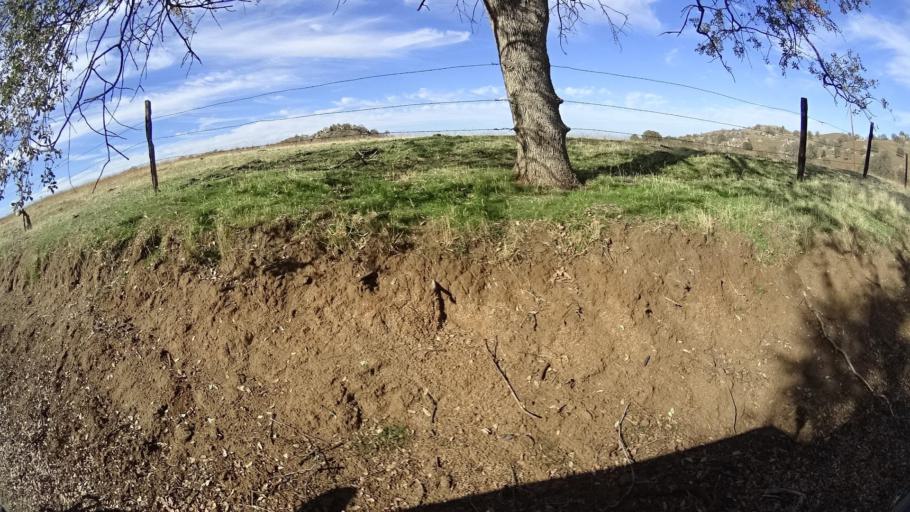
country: US
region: California
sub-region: Kern County
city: Oildale
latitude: 35.5785
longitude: -118.8118
